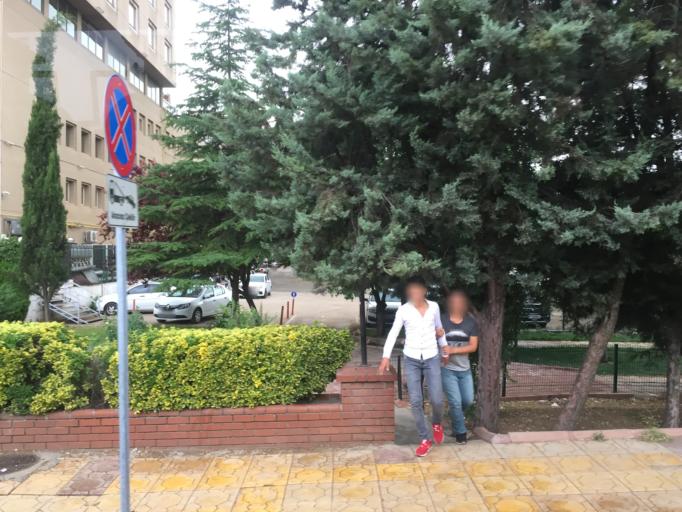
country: TR
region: Gaziantep
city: Gaziantep
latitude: 37.0730
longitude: 37.3721
